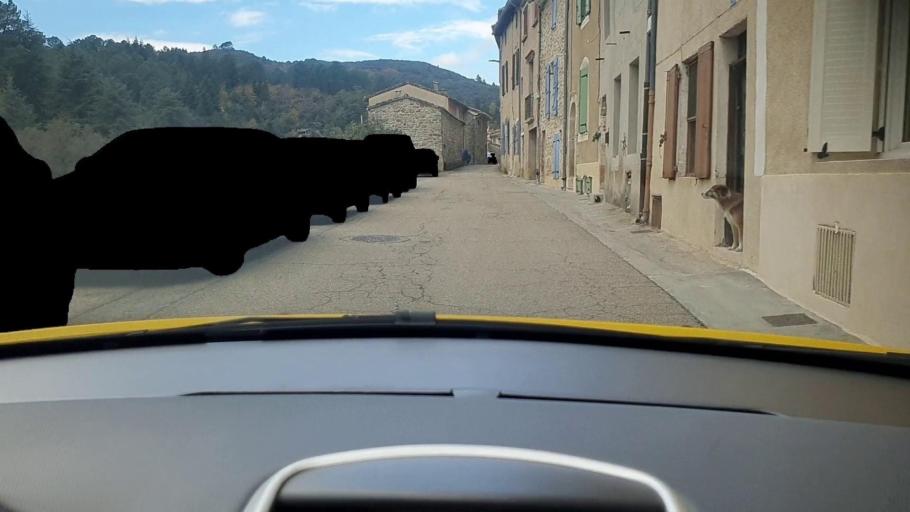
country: FR
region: Languedoc-Roussillon
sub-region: Departement du Gard
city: Lasalle
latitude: 44.0483
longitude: 3.8463
